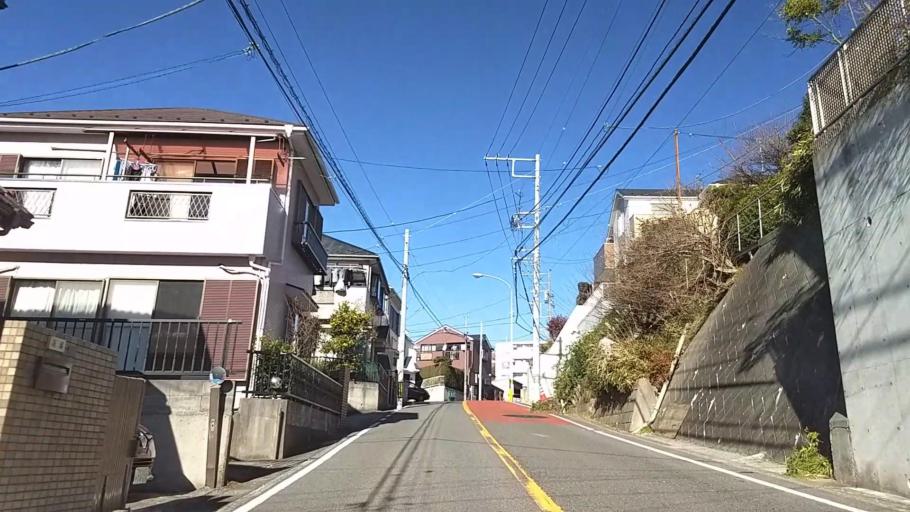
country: JP
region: Kanagawa
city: Yokohama
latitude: 35.4485
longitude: 139.5890
